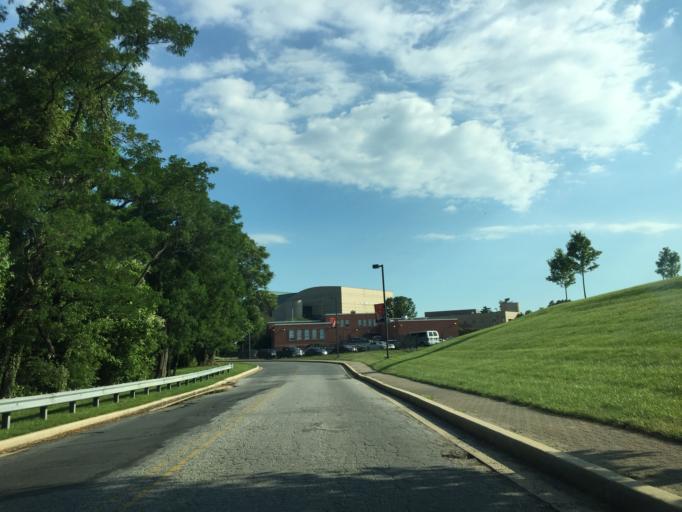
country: US
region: Maryland
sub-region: Baltimore County
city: Parkville
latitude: 39.3422
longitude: -76.5823
